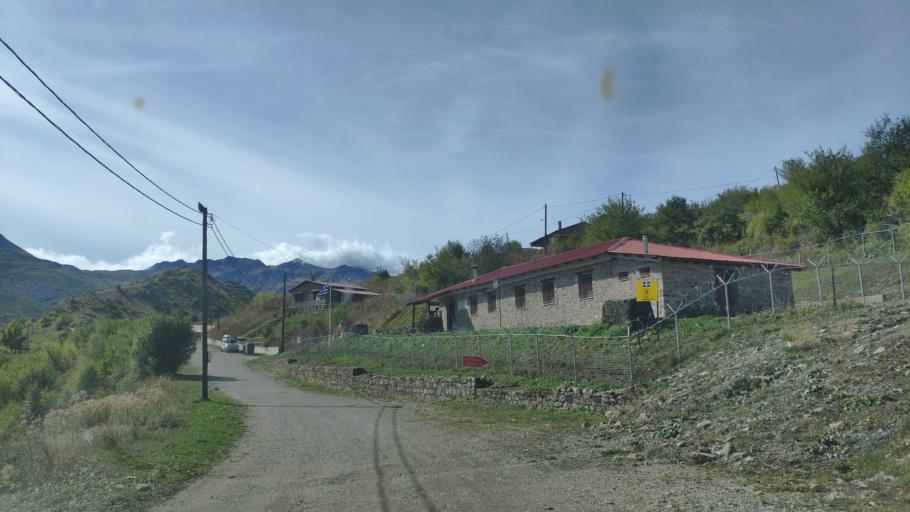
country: AL
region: Korce
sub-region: Rrethi i Devollit
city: Miras
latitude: 40.3932
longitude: 20.8361
